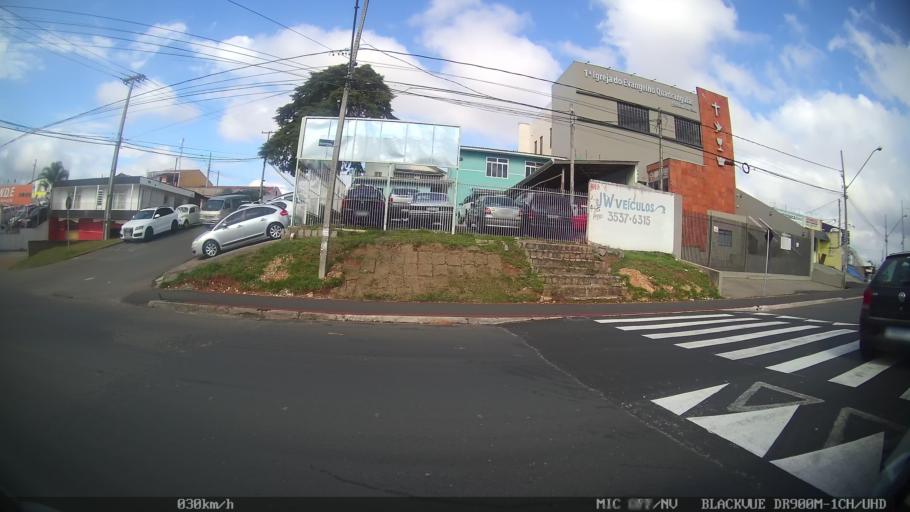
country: BR
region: Parana
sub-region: Pinhais
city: Pinhais
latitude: -25.3693
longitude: -49.1860
